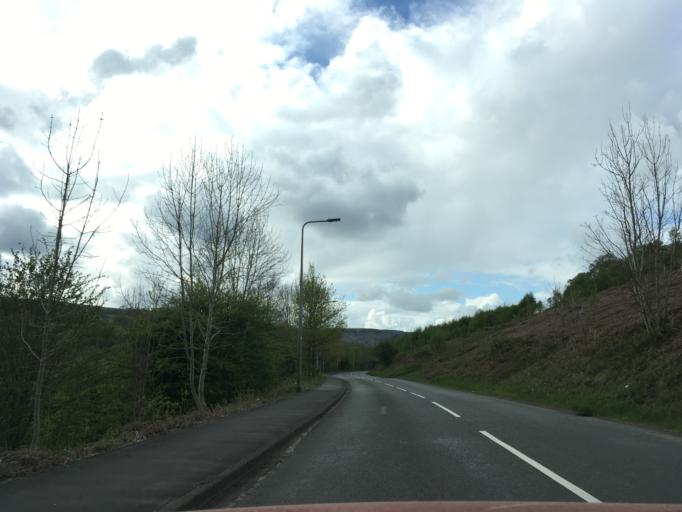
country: GB
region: Wales
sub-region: Merthyr Tydfil County Borough
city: Treharris
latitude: 51.6918
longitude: -3.3025
